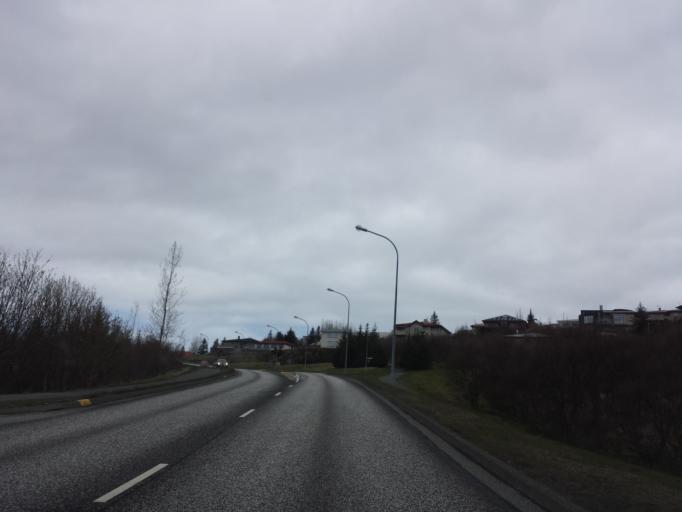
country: IS
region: Capital Region
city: Kopavogur
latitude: 64.1072
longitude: -21.8822
